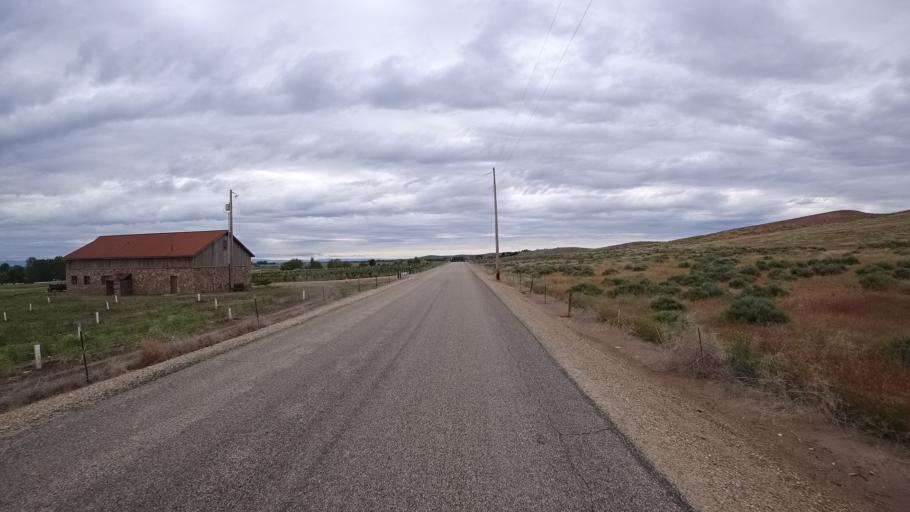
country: US
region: Idaho
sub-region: Ada County
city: Eagle
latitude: 43.7355
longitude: -116.4058
